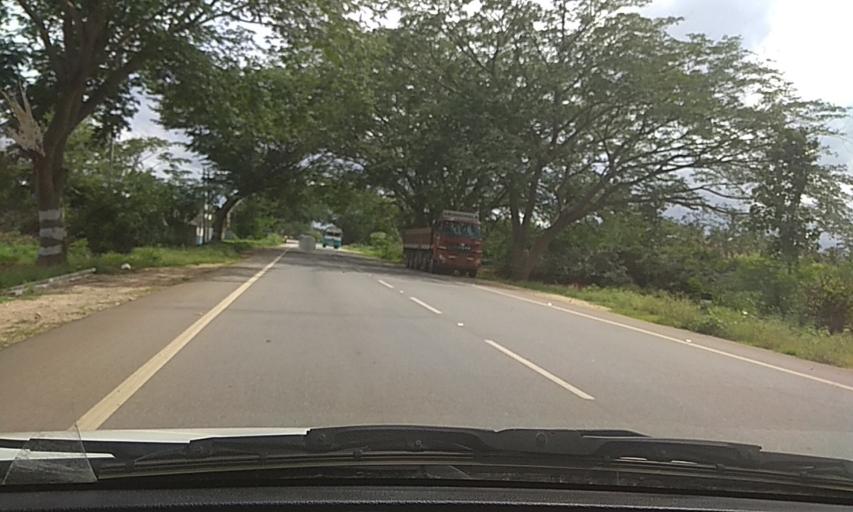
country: IN
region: Karnataka
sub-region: Tumkur
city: Tumkur
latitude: 13.2409
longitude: 77.0763
